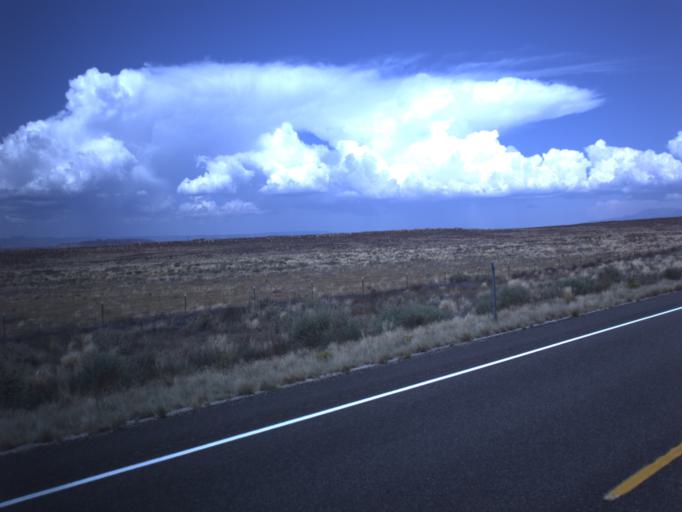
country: US
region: Utah
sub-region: San Juan County
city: Blanding
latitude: 37.3234
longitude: -109.5225
